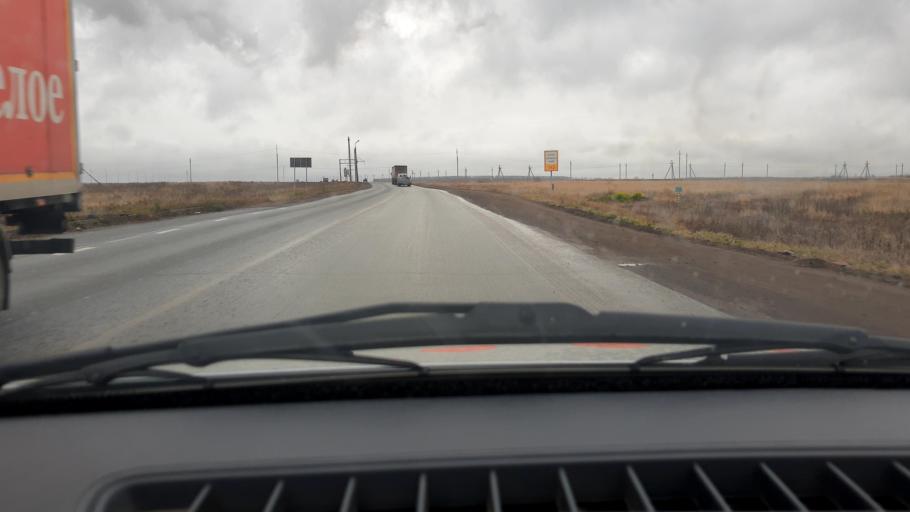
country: RU
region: Bashkortostan
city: Iglino
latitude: 54.7660
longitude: 56.2634
